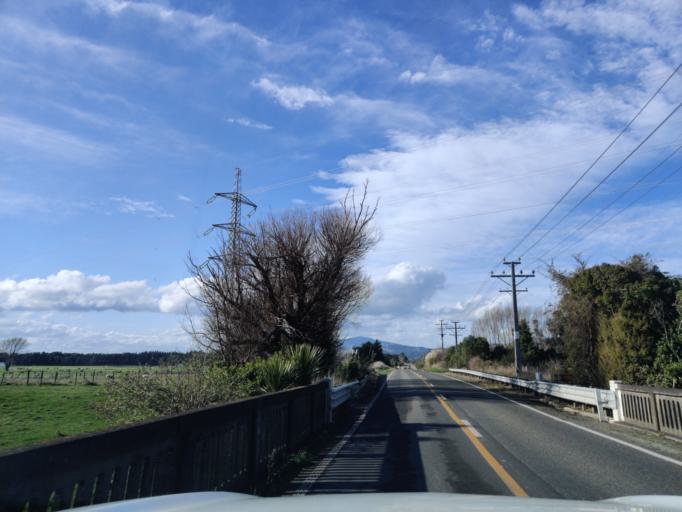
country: NZ
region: Manawatu-Wanganui
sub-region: Palmerston North City
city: Palmerston North
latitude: -40.3442
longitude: 175.7108
